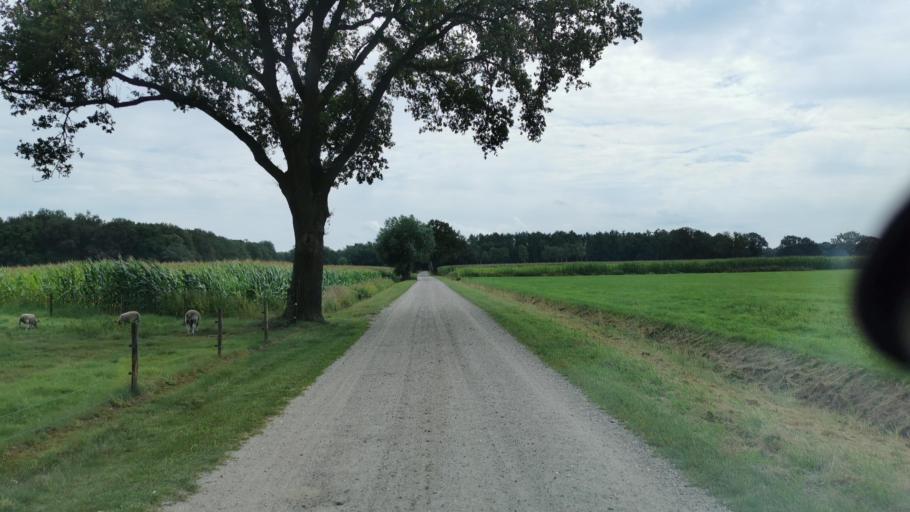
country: NL
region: Overijssel
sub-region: Gemeente Losser
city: Losser
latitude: 52.2530
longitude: 6.9555
